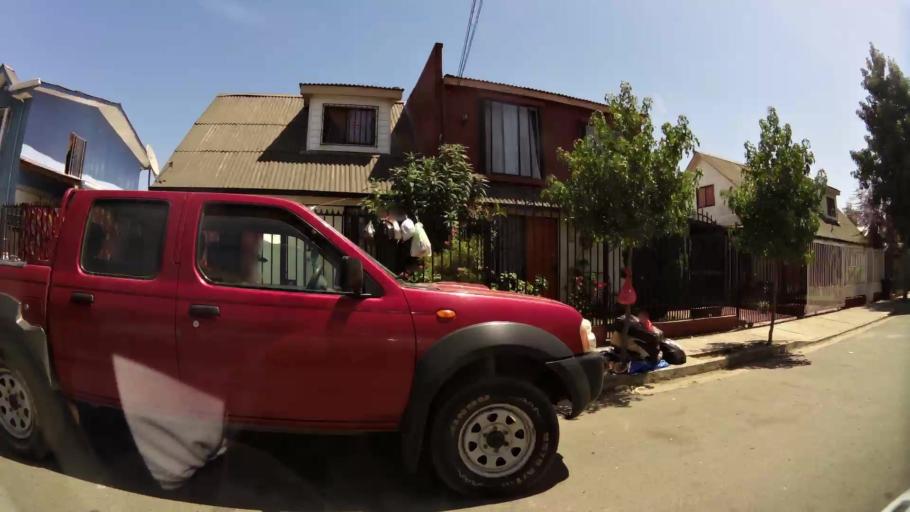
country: CL
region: Maule
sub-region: Provincia de Talca
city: Talca
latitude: -35.4343
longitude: -71.6331
